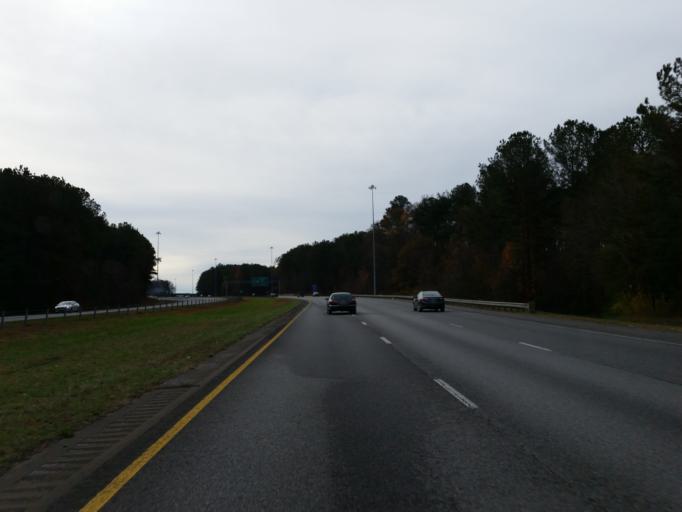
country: US
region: Georgia
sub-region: Cherokee County
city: Canton
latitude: 34.2473
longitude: -84.4676
